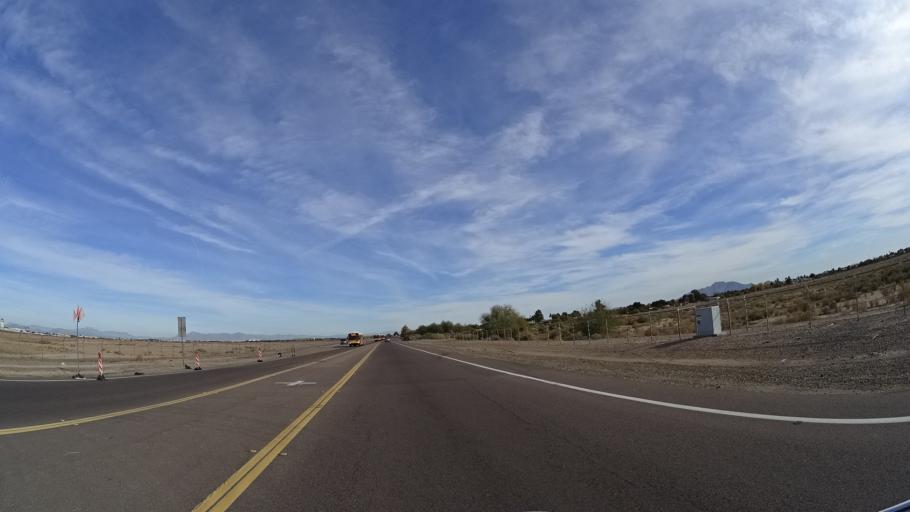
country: US
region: Arizona
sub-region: Maricopa County
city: Chandler
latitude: 33.2624
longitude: -111.8201
